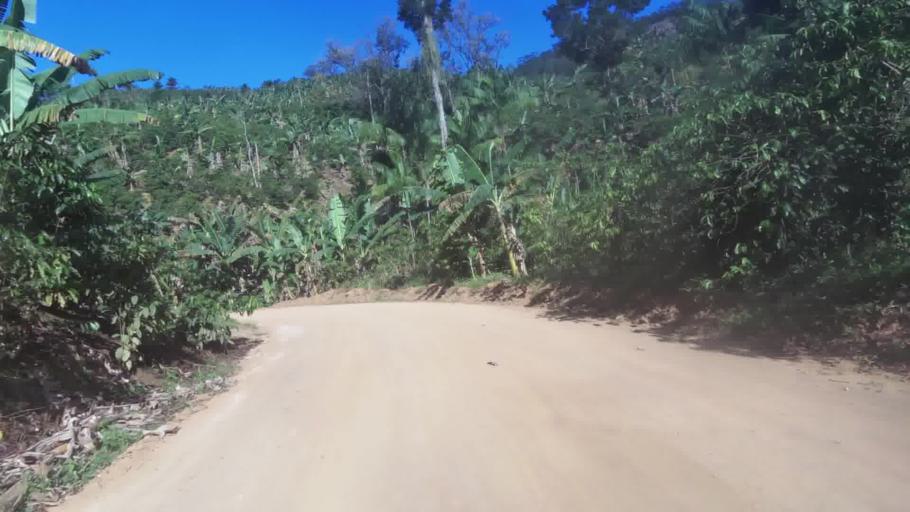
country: BR
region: Espirito Santo
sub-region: Iconha
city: Iconha
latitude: -20.7567
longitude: -40.8163
